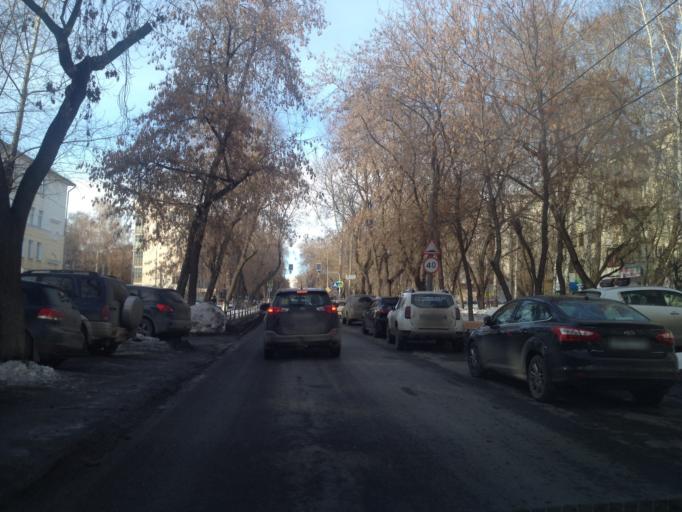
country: RU
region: Sverdlovsk
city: Yekaterinburg
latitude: 56.8376
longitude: 60.6273
